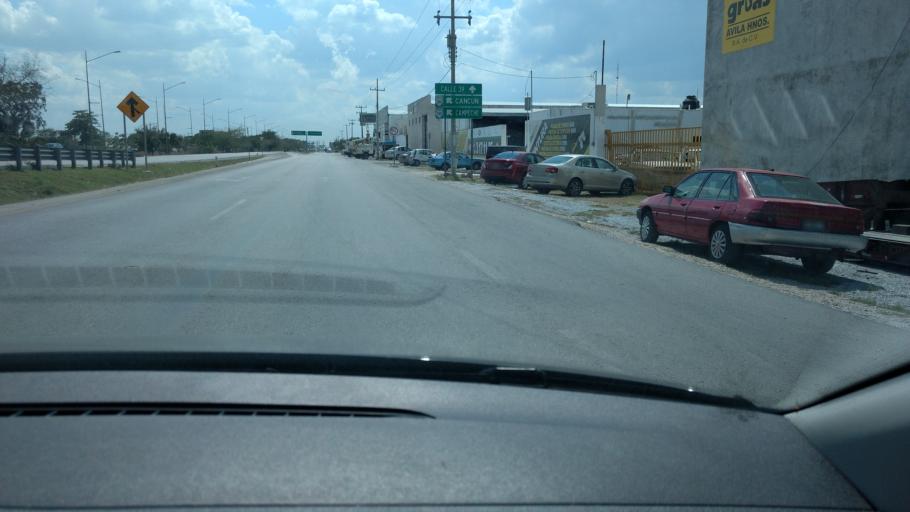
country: MX
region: Yucatan
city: Merida
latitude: 20.9966
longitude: -89.5620
